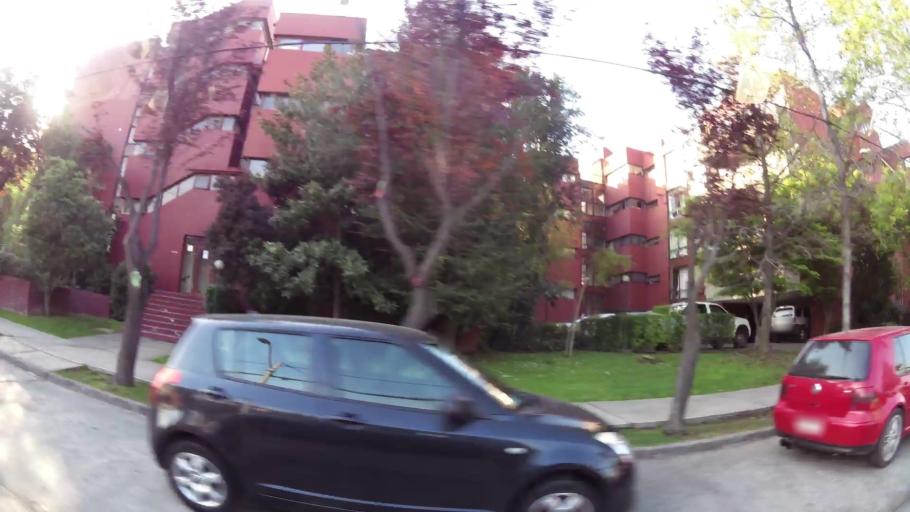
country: CL
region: Santiago Metropolitan
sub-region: Provincia de Santiago
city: Villa Presidente Frei, Nunoa, Santiago, Chile
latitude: -33.3845
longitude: -70.5440
